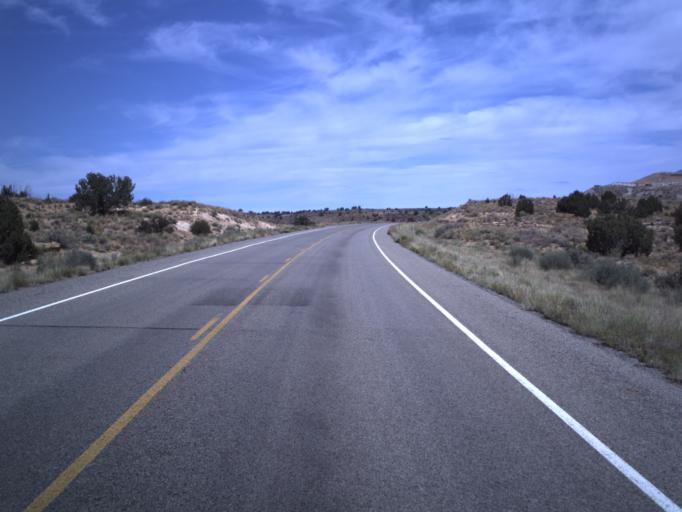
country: US
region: Colorado
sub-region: Montezuma County
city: Towaoc
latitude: 37.1851
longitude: -109.1266
